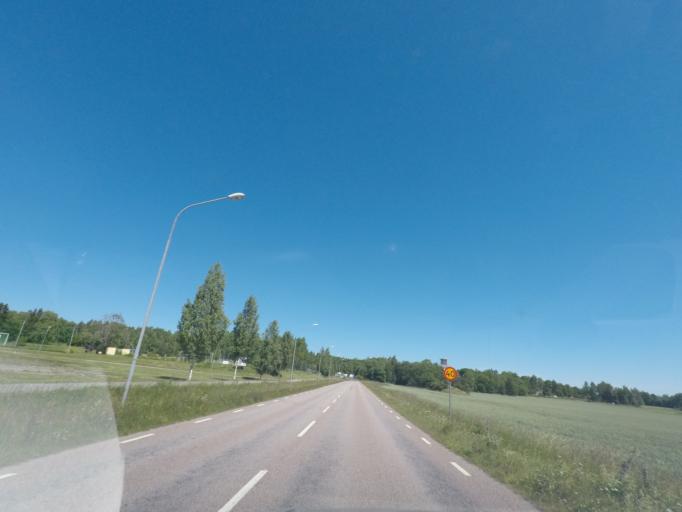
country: SE
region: Vaestmanland
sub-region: Vasteras
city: Tillberga
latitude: 59.6746
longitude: 16.7261
